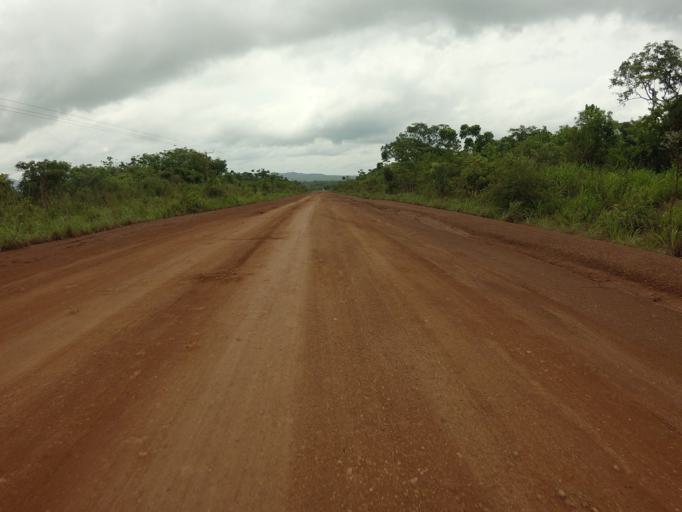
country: GH
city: Kpandae
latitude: 8.3038
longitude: 0.4854
